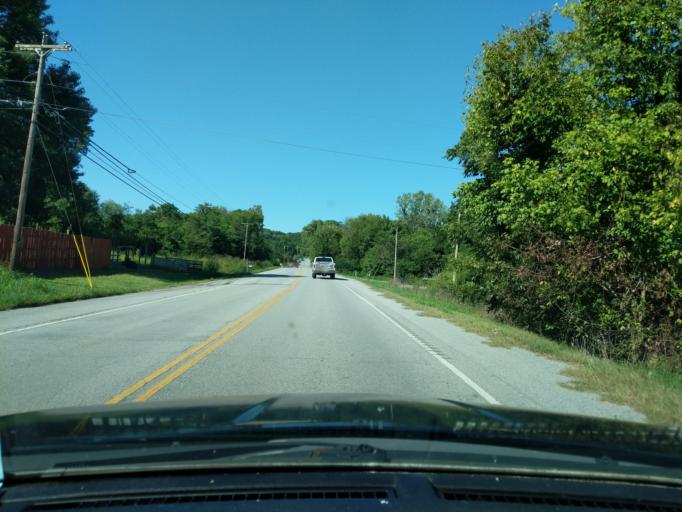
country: US
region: Tennessee
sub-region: Smith County
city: Carthage
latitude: 36.2508
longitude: -86.0164
